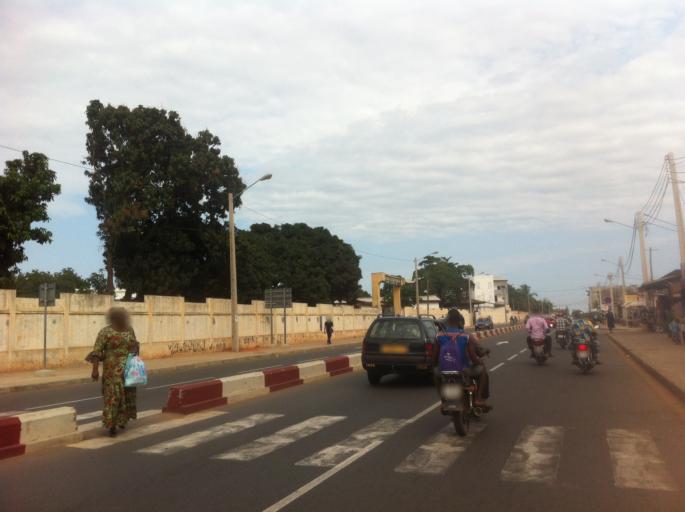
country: TG
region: Maritime
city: Lome
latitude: 6.1452
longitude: 1.2050
